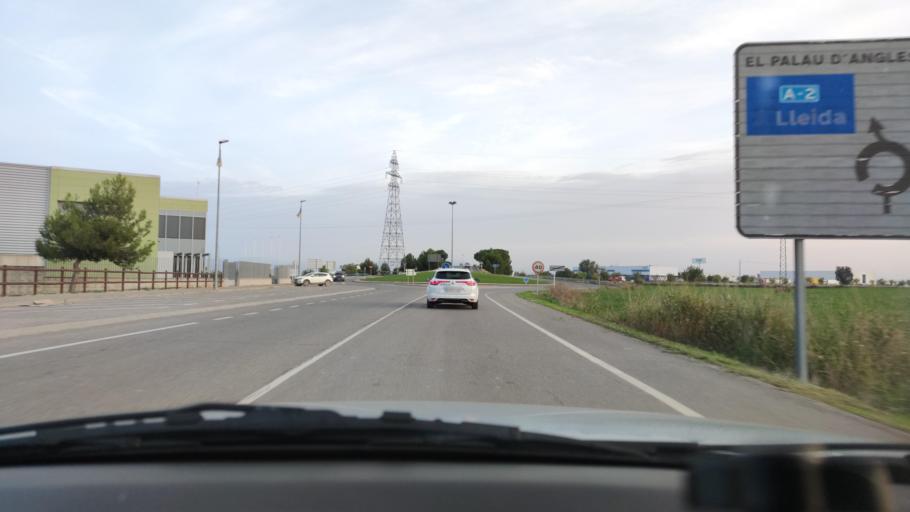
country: ES
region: Catalonia
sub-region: Provincia de Lleida
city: Mollerussa
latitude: 41.6370
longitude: 0.8749
